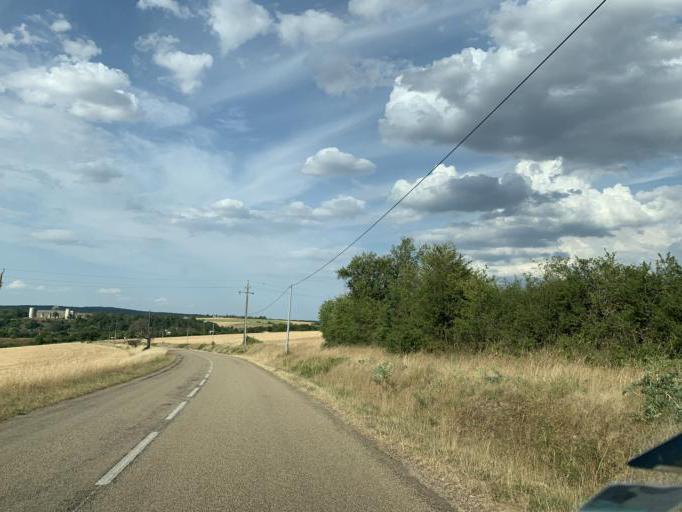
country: FR
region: Bourgogne
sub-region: Departement de l'Yonne
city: Fontenailles
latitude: 47.5405
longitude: 3.4162
